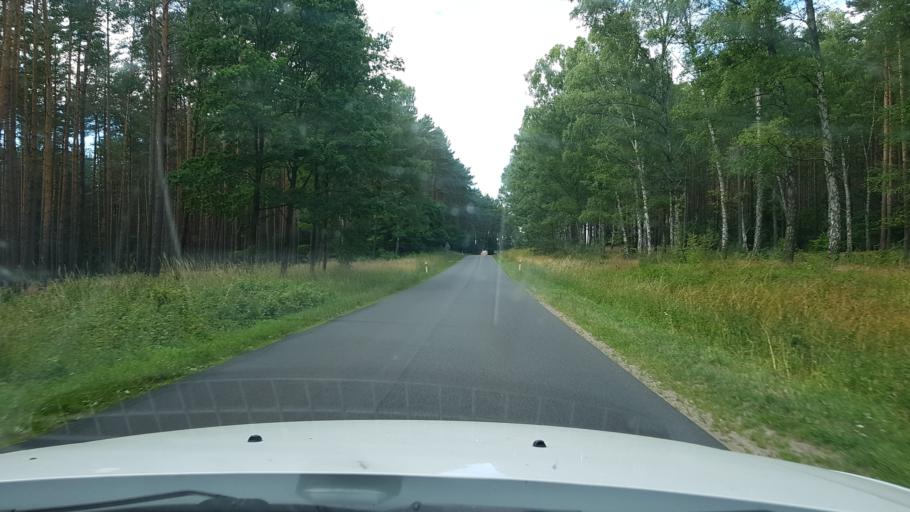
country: PL
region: West Pomeranian Voivodeship
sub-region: Powiat drawski
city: Zlocieniec
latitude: 53.5156
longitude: 16.0216
